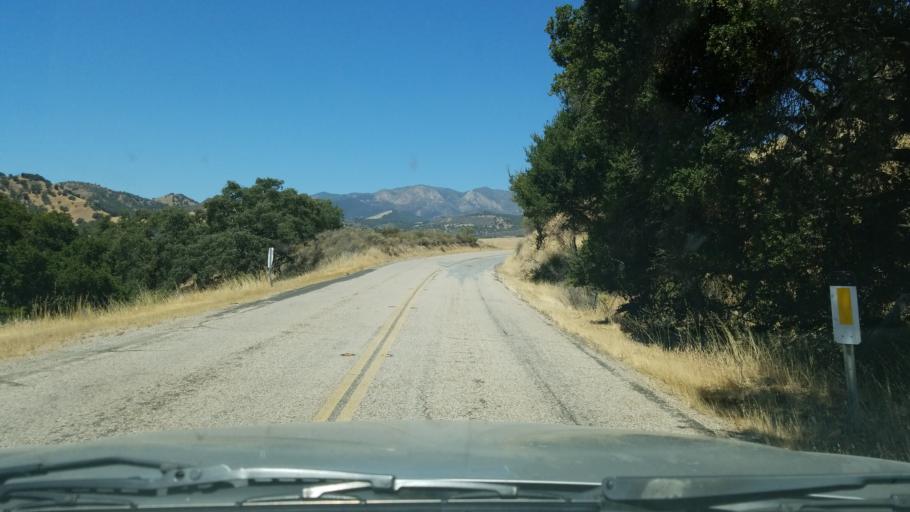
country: US
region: California
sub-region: Monterey County
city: Greenfield
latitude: 36.2662
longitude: -121.3673
